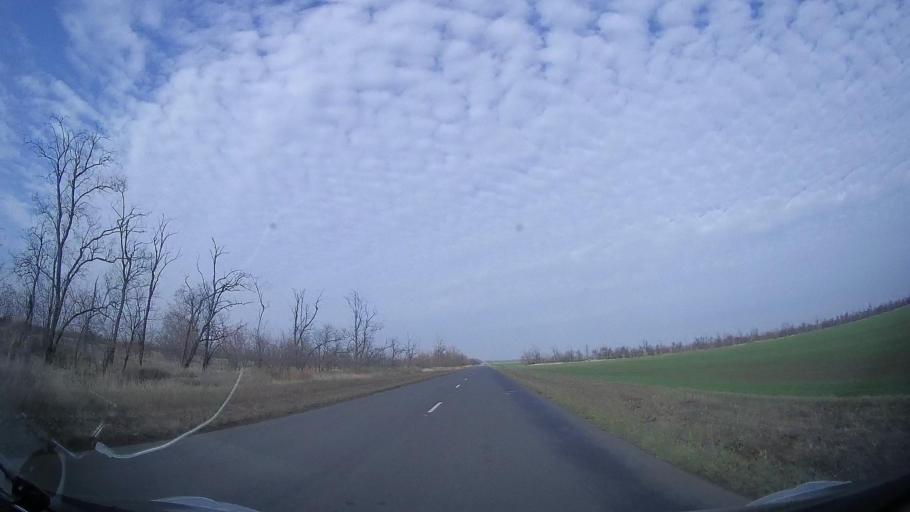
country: RU
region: Rostov
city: Gigant
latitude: 46.8581
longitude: 41.2810
